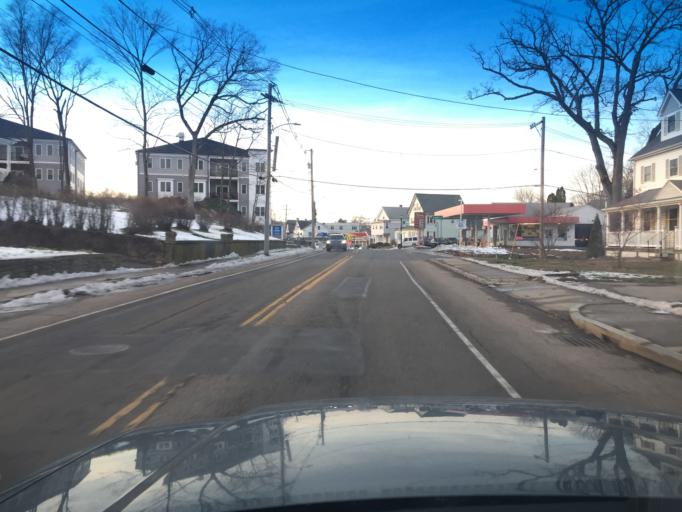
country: US
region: Massachusetts
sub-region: Norfolk County
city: Franklin
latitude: 42.0815
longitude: -71.3930
